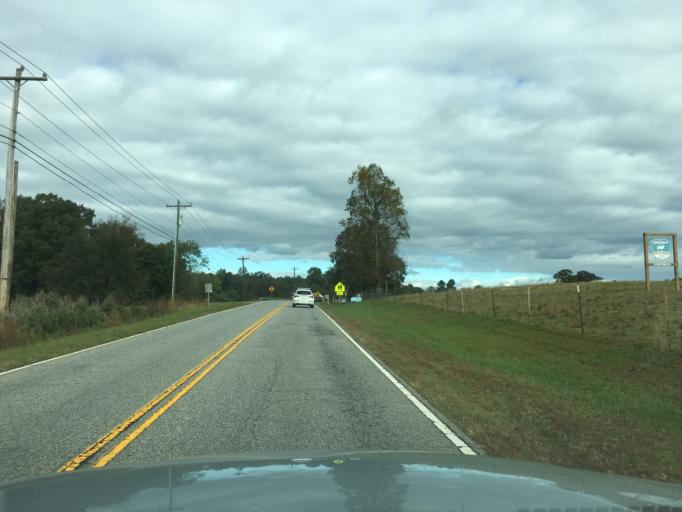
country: US
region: South Carolina
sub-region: Greenville County
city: Tigerville
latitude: 35.0390
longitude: -82.2667
